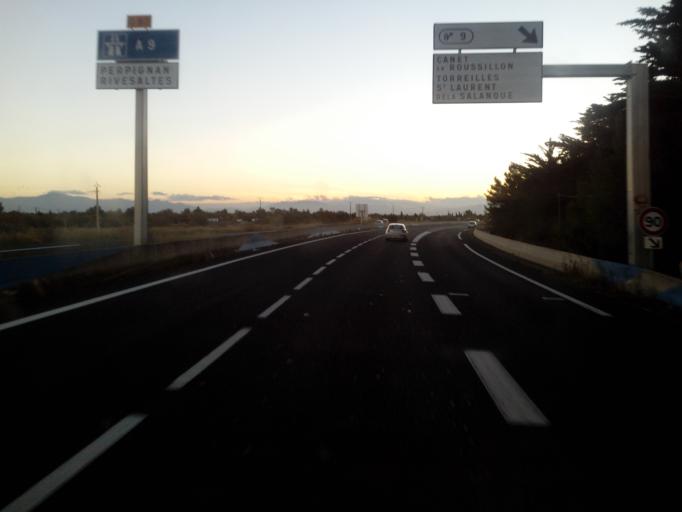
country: FR
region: Languedoc-Roussillon
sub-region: Departement des Pyrenees-Orientales
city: Le Barcares
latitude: 42.7897
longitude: 3.0230
